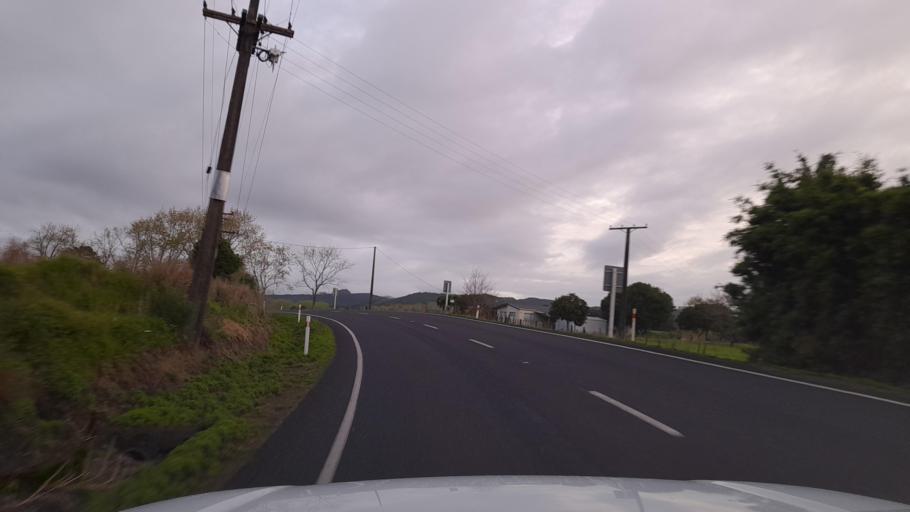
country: NZ
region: Northland
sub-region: Whangarei
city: Maungatapere
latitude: -35.7296
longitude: 174.0468
